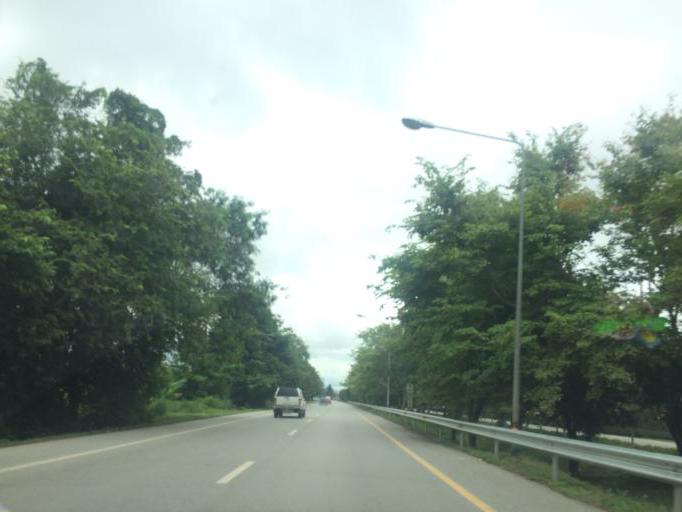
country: TH
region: Chiang Rai
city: Chiang Rai
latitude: 19.8550
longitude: 99.8145
